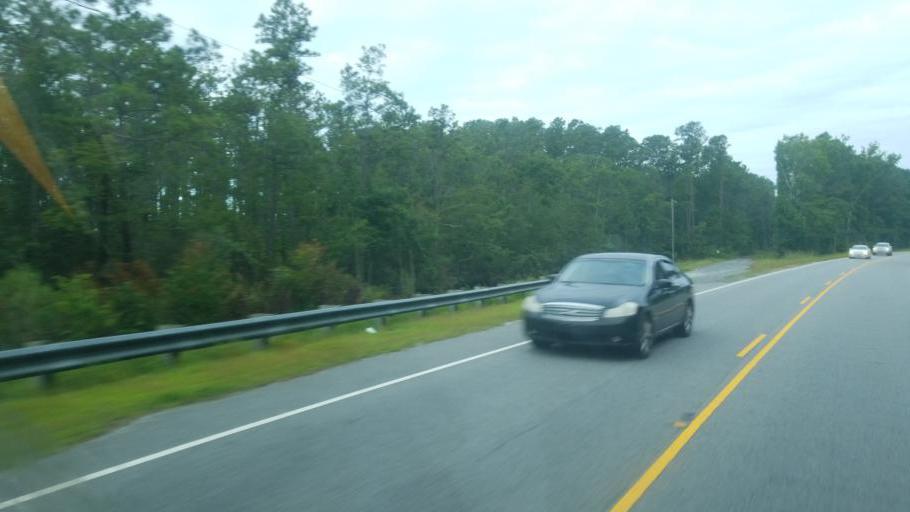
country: US
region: North Carolina
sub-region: Dare County
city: Manteo
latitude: 35.8674
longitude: -75.9132
